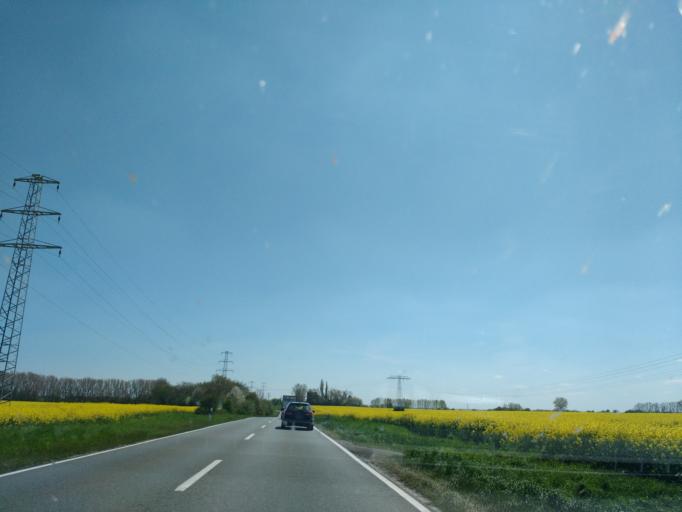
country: DE
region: Saxony-Anhalt
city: Deuben
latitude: 51.1072
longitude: 12.0904
